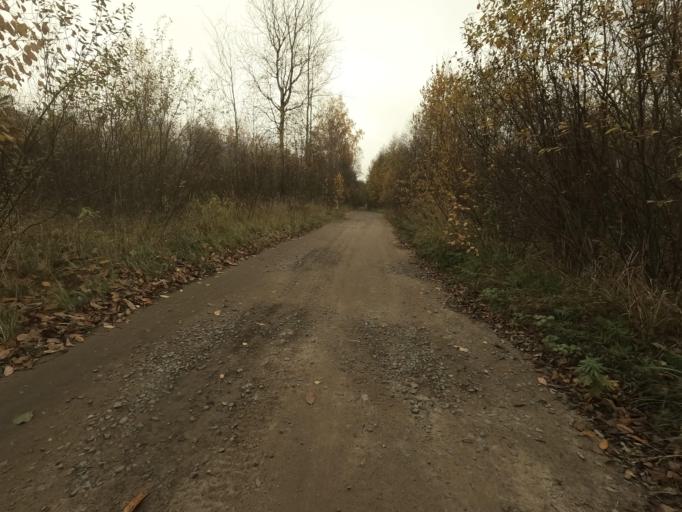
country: RU
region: Leningrad
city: Pavlovo
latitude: 59.7898
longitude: 30.8824
